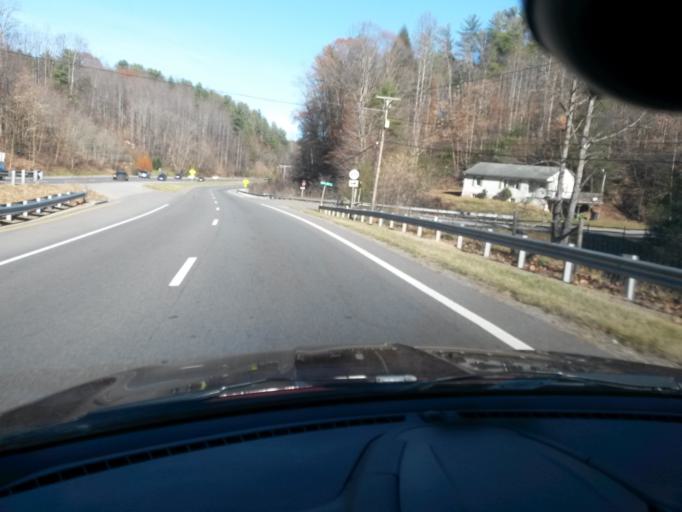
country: US
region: Virginia
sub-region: Roanoke County
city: Narrows
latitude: 37.1632
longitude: -79.9461
